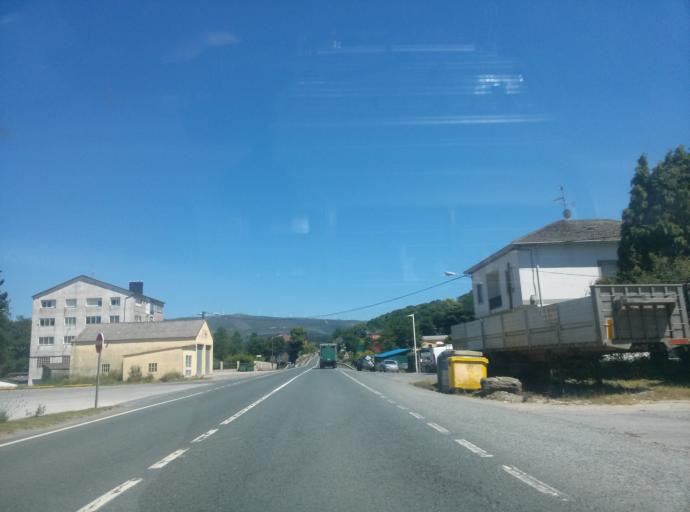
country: ES
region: Galicia
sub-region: Provincia de Lugo
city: Meira
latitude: 43.2155
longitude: -7.3091
